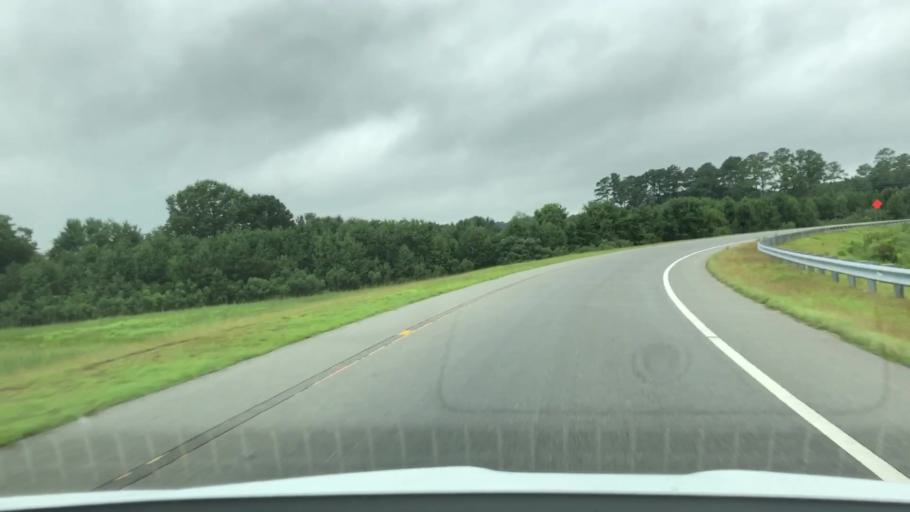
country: US
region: North Carolina
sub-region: Wayne County
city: Goldsboro
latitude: 35.4275
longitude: -77.9887
